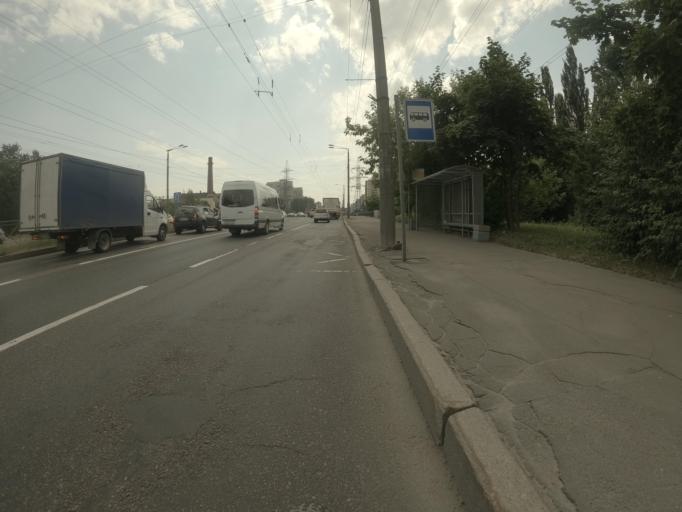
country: RU
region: St.-Petersburg
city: Krasnogvargeisky
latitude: 59.9589
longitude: 30.4634
